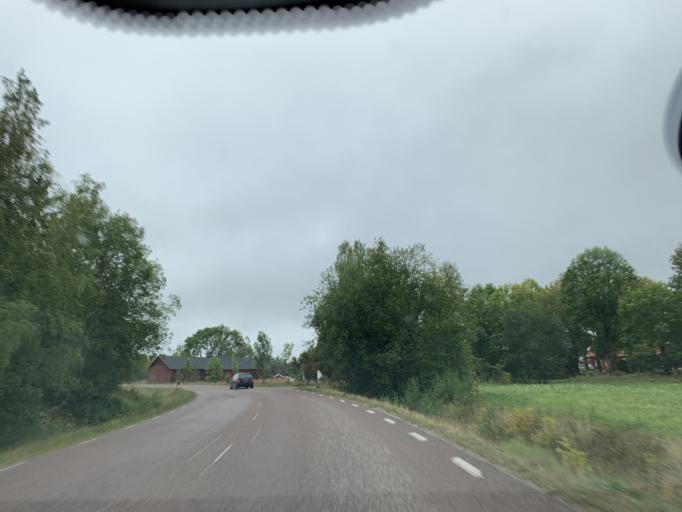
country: SE
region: Soedermanland
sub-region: Eskilstuna Kommun
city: Kvicksund
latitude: 59.5602
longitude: 16.4083
